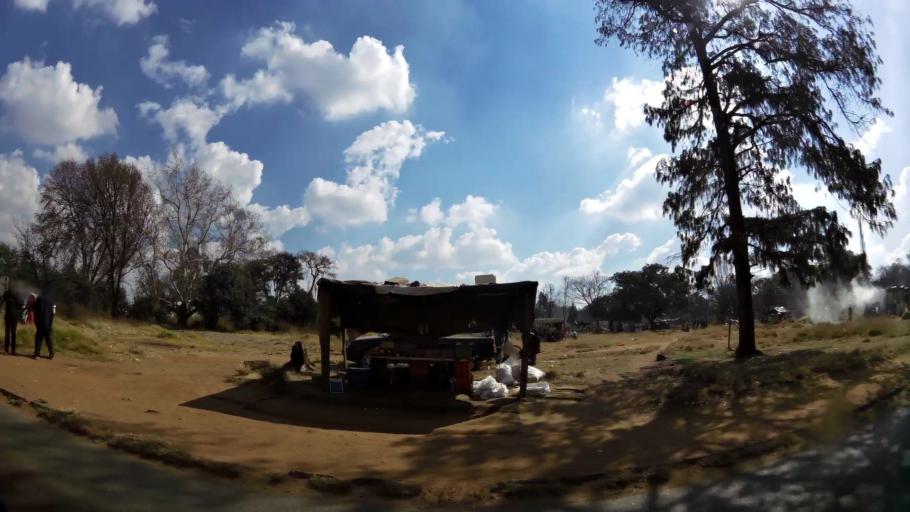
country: ZA
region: Gauteng
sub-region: City of Johannesburg Metropolitan Municipality
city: Roodepoort
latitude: -26.1758
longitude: 27.8723
